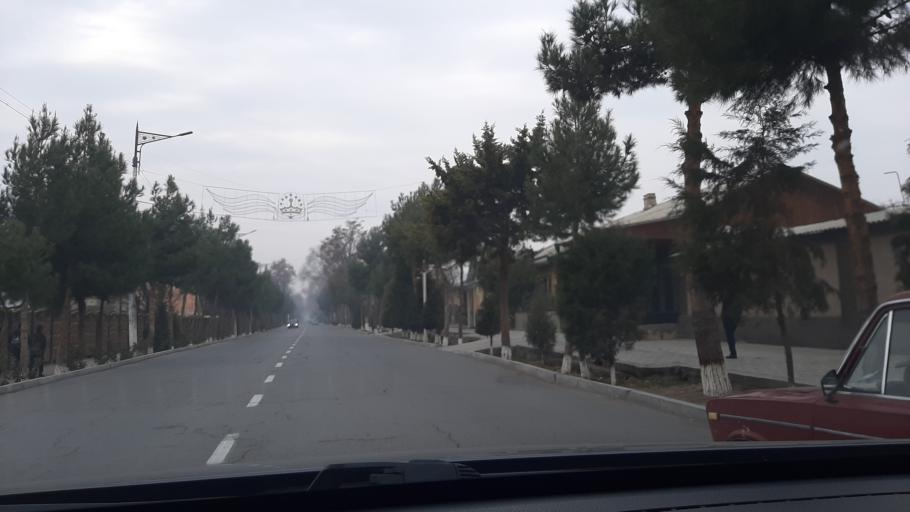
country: TJ
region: Viloyati Sughd
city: Palos
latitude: 40.2637
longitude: 69.7920
